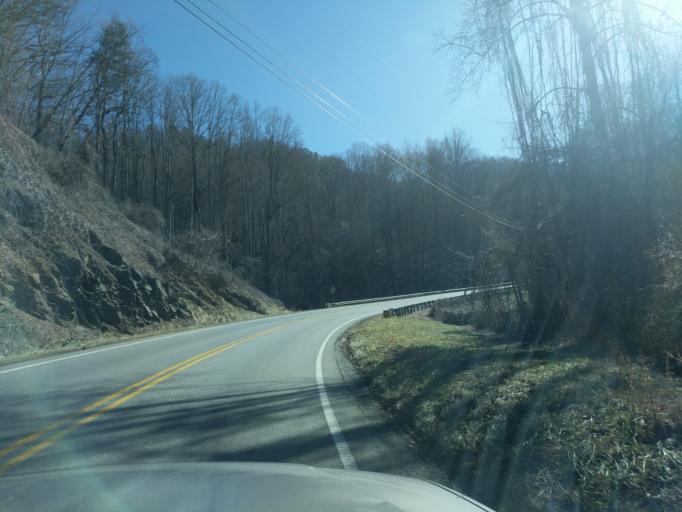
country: US
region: North Carolina
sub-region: Swain County
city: Bryson City
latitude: 35.3588
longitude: -83.5525
